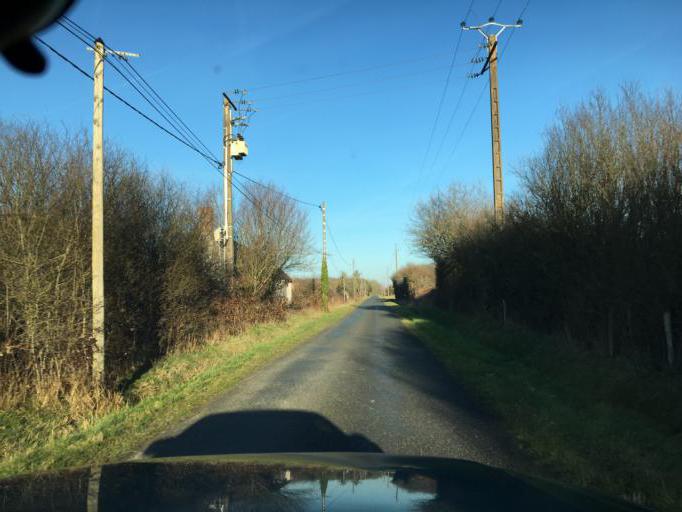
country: FR
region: Centre
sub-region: Departement du Loiret
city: Ligny-le-Ribault
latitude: 47.7044
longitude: 1.7568
